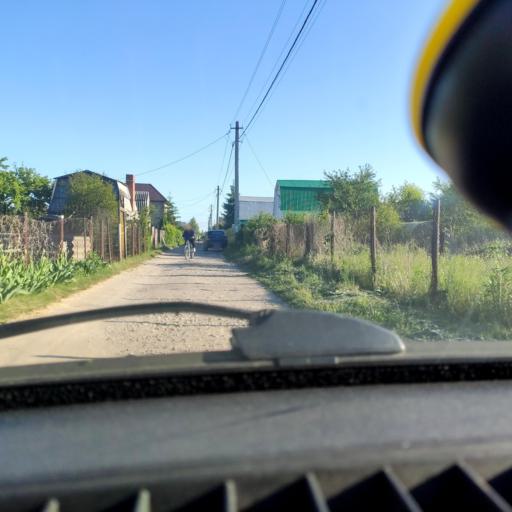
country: RU
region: Samara
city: Tol'yatti
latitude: 53.5923
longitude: 49.3150
